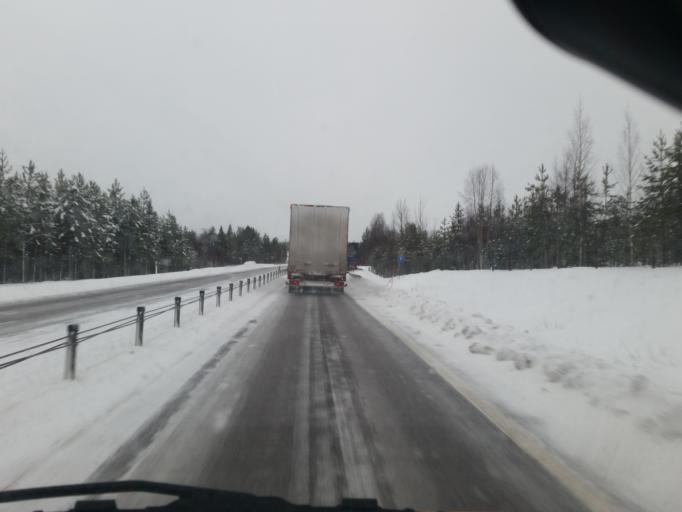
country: SE
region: Norrbotten
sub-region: Pitea Kommun
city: Pitea
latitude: 65.2050
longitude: 21.5179
